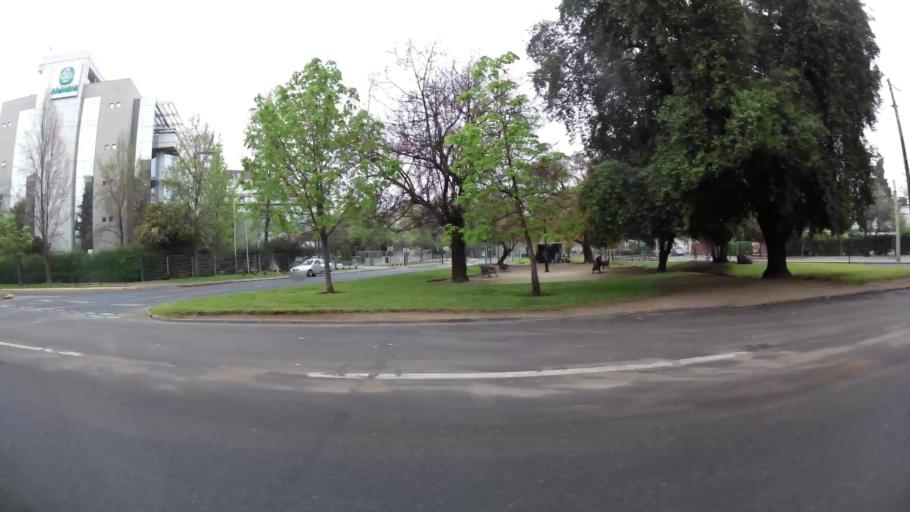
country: CL
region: Santiago Metropolitan
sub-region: Provincia de Santiago
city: Villa Presidente Frei, Nunoa, Santiago, Chile
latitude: -33.3910
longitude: -70.5729
